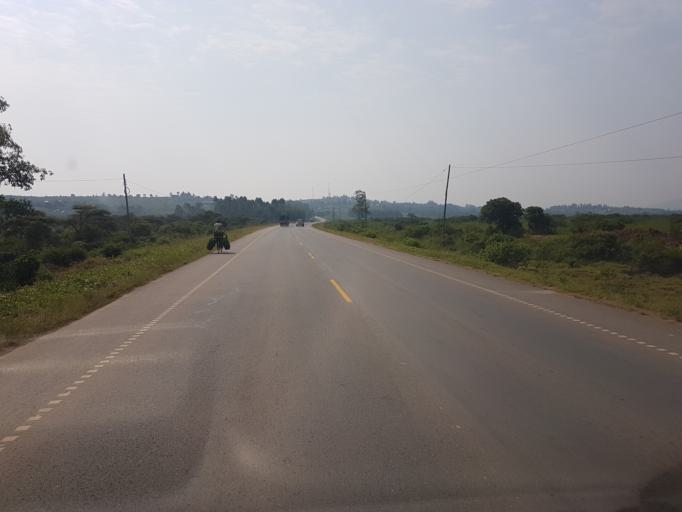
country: UG
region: Western Region
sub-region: Mbarara District
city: Bwizibwera
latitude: -0.6423
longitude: 30.5770
